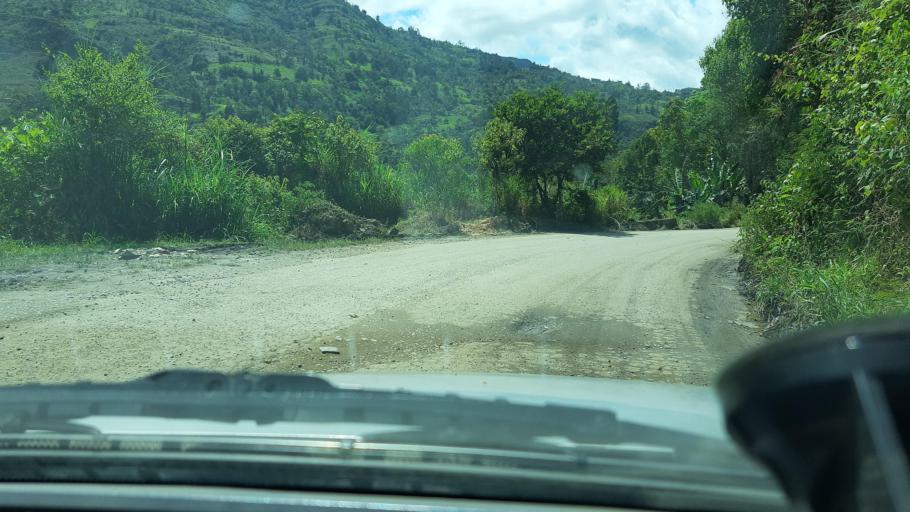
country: CO
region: Boyaca
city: Chinavita
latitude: 5.1761
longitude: -73.3818
